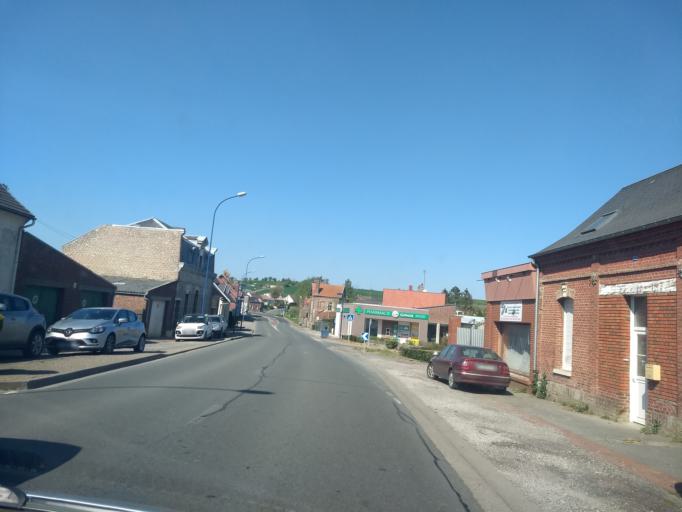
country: FR
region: Picardie
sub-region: Departement de la Somme
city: Beauval
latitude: 50.1134
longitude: 2.3397
